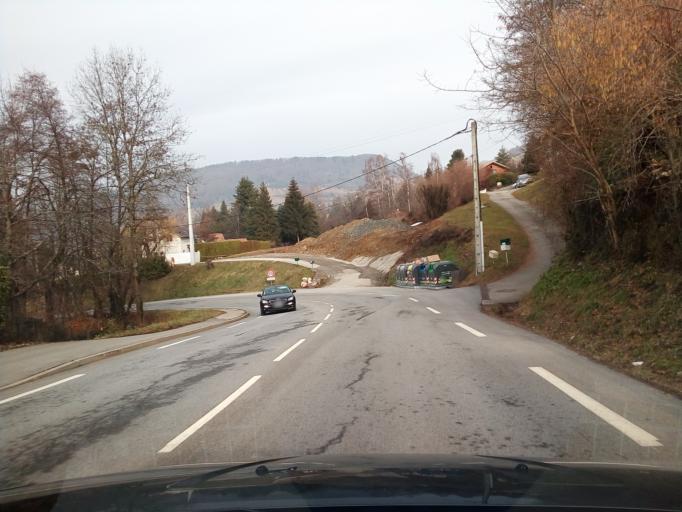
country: FR
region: Rhone-Alpes
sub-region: Departement de l'Isere
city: Revel
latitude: 45.1509
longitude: 5.8434
